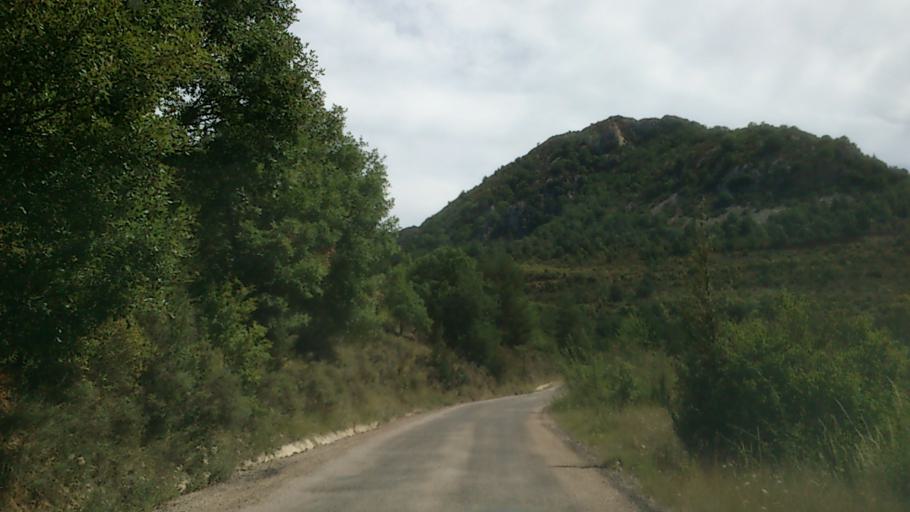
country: ES
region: Aragon
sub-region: Provincia de Huesca
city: Arguis
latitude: 42.3152
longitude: -0.3221
